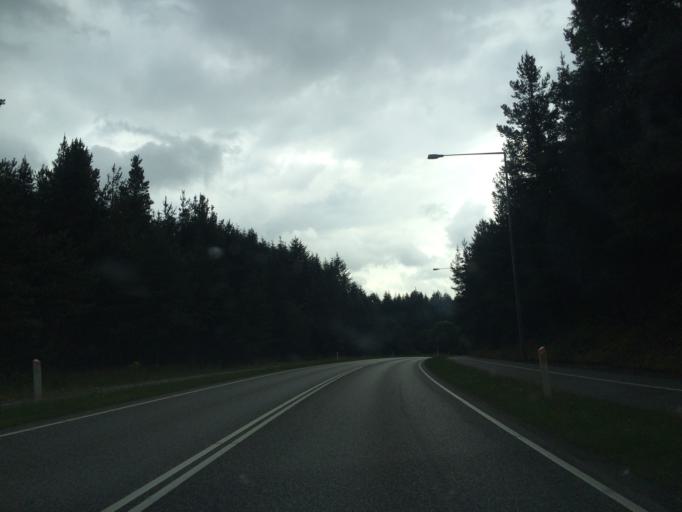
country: DK
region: Central Jutland
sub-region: Silkeborg Kommune
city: Silkeborg
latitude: 56.1672
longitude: 9.5266
